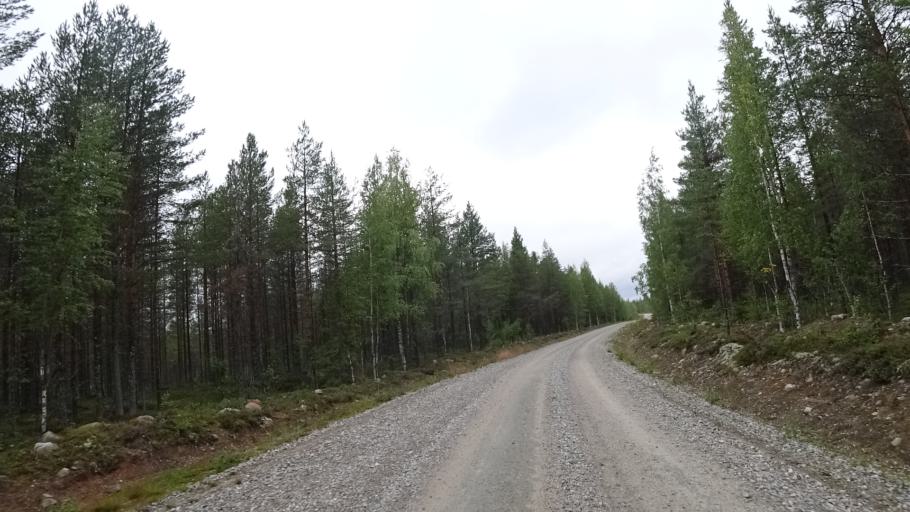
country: FI
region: North Karelia
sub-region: Pielisen Karjala
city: Lieksa
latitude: 63.4695
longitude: 30.2778
